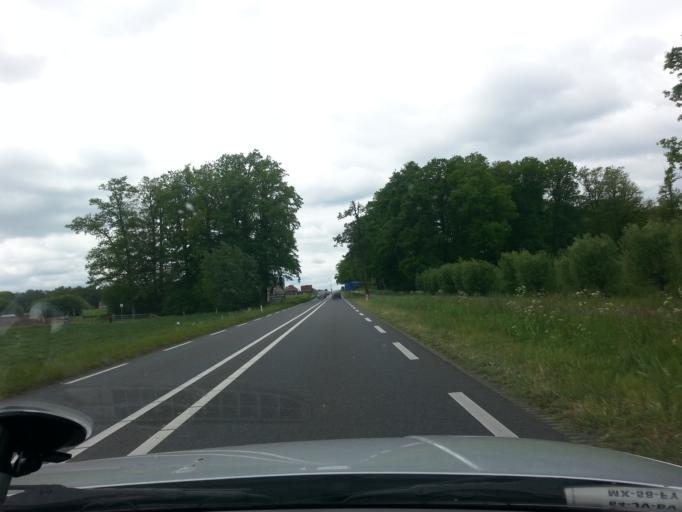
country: NL
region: Overijssel
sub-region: Gemeente Oldenzaal
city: Oldenzaal
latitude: 52.3253
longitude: 6.9442
